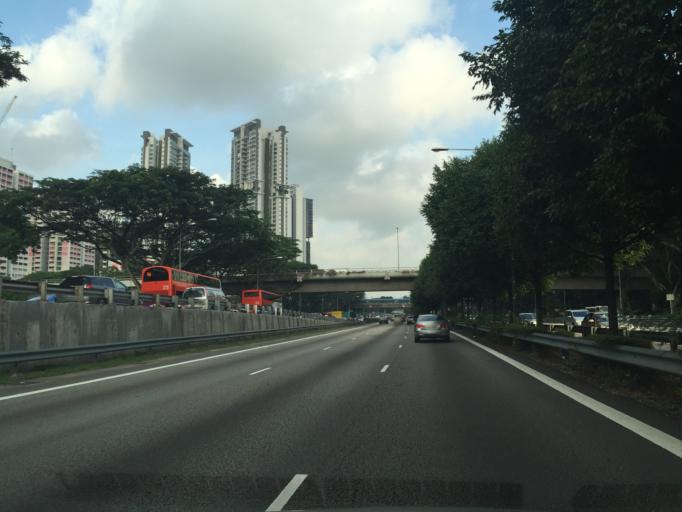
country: SG
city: Singapore
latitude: 1.3296
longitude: 103.8467
